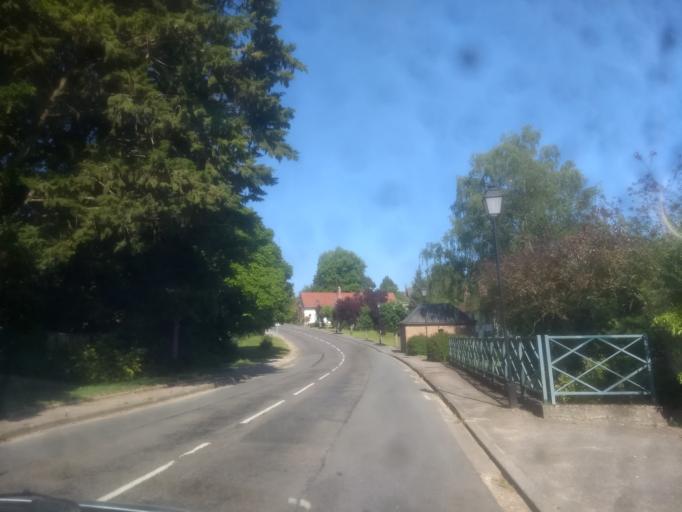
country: FR
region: Picardie
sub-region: Departement de la Somme
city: Saint-Riquier
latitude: 50.1693
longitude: 1.8785
